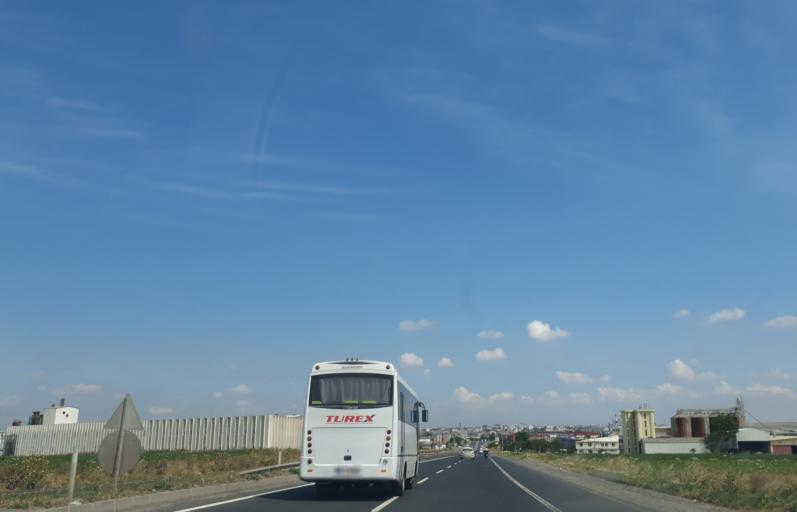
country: TR
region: Tekirdag
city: Marmaracik
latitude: 41.2546
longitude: 27.6753
